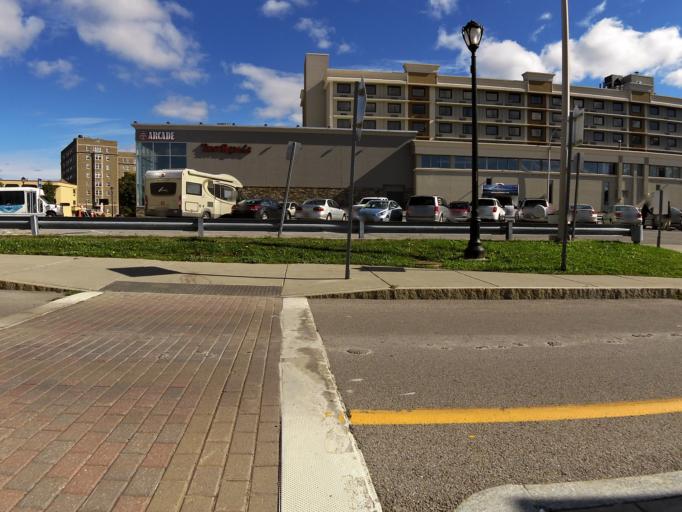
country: US
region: New York
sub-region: Niagara County
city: Niagara Falls
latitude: 43.0844
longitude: -79.0618
